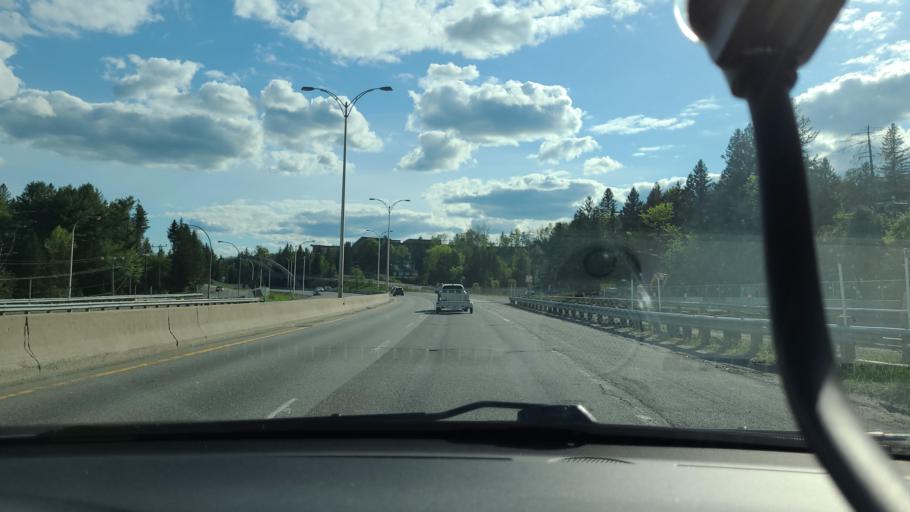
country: CA
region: Quebec
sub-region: Laurentides
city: Sainte-Adele
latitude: 45.9404
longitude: -74.1291
